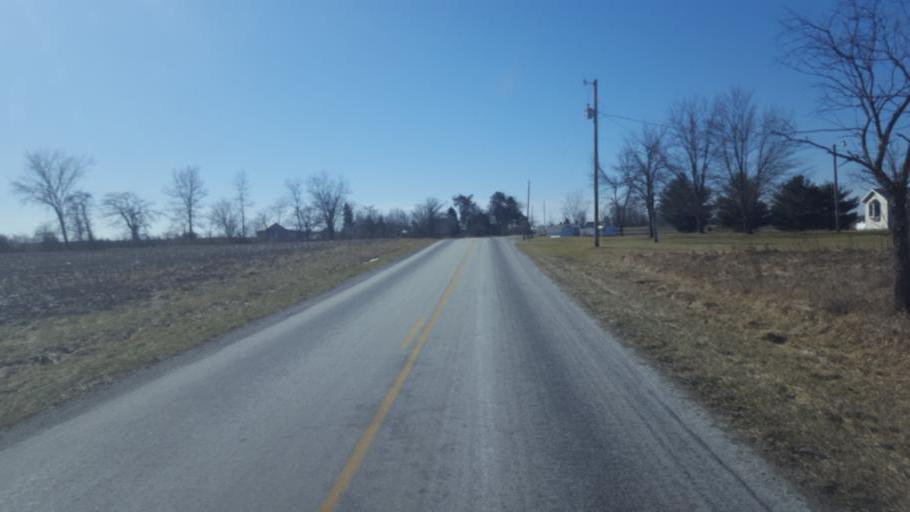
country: US
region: Ohio
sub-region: Hardin County
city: Kenton
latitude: 40.6404
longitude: -83.4747
